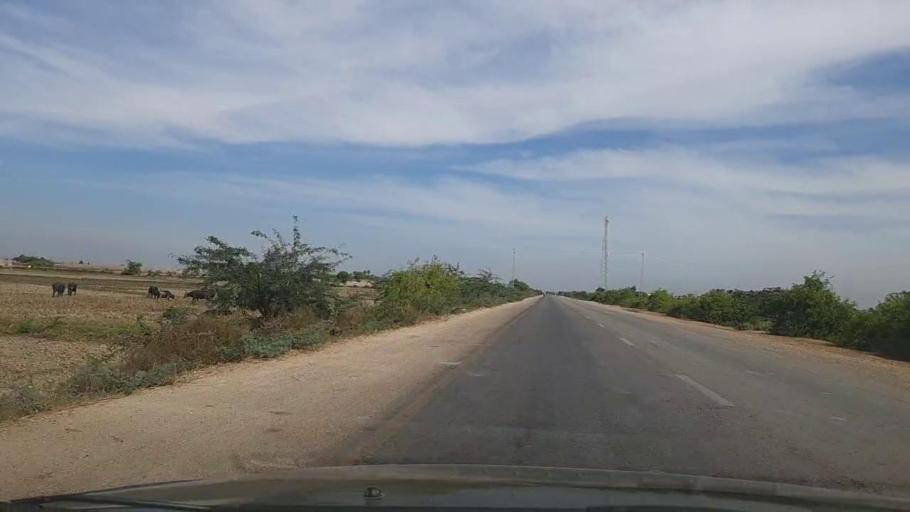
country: PK
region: Sindh
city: Thatta
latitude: 24.8088
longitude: 67.9736
